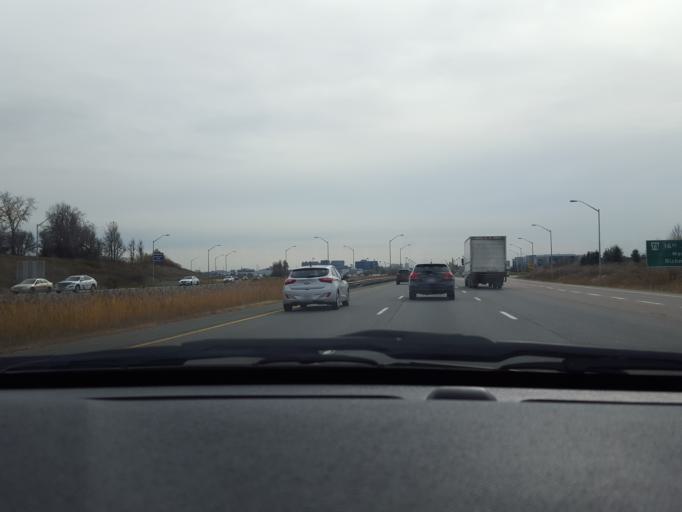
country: CA
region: Ontario
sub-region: York
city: Richmond Hill
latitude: 43.8703
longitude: -79.3768
